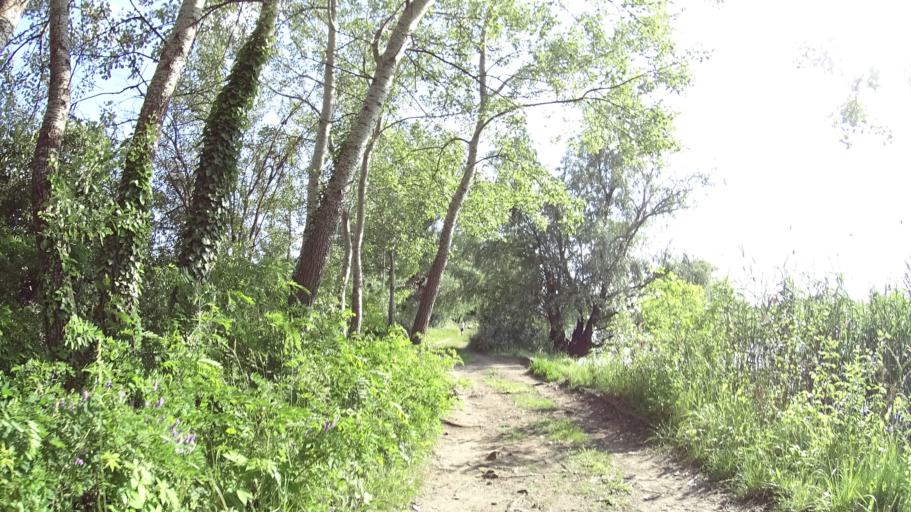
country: HU
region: Pest
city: Dunaharaszti
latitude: 47.3641
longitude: 19.0880
